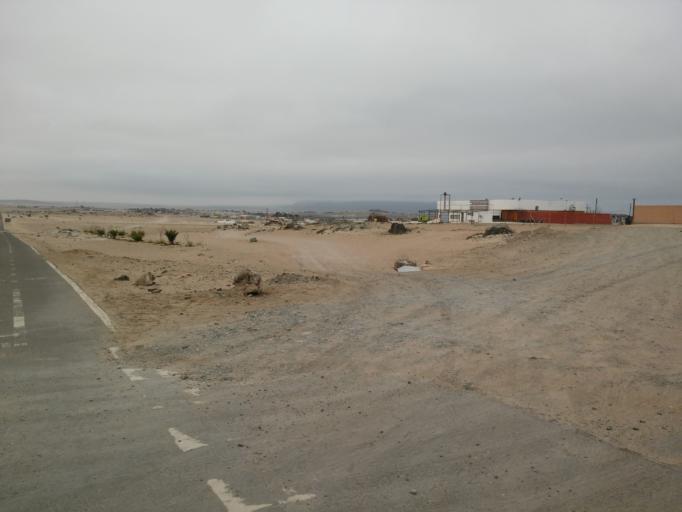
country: CL
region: Atacama
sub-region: Provincia de Copiapo
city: Copiapo
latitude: -27.0776
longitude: -70.8335
